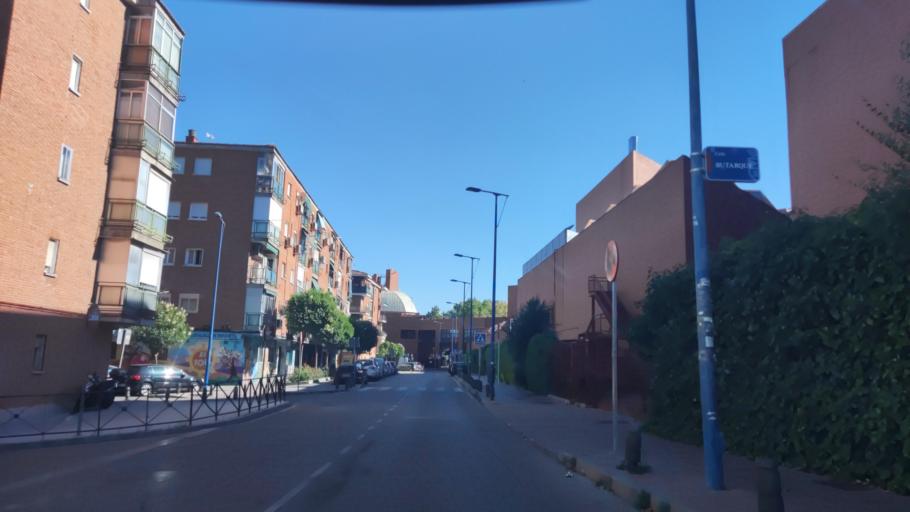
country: ES
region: Madrid
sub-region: Provincia de Madrid
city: Leganes
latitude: 40.3343
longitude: -3.7658
